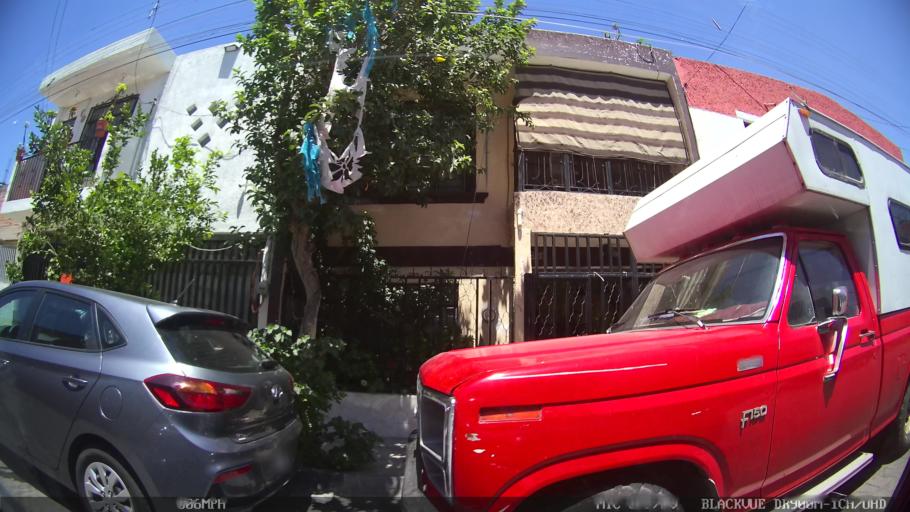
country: MX
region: Jalisco
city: Tlaquepaque
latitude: 20.6557
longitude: -103.2777
